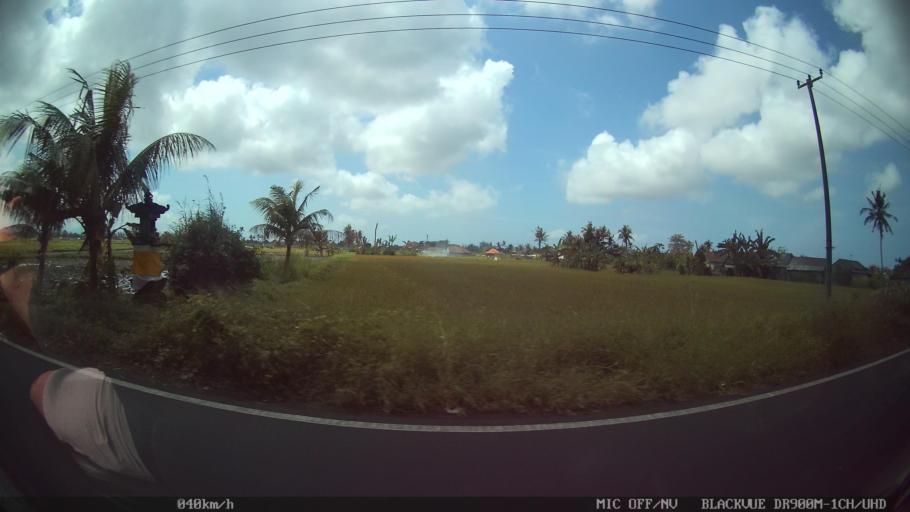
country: ID
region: Bali
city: Banjar Pasekan
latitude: -8.5797
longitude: 115.2953
